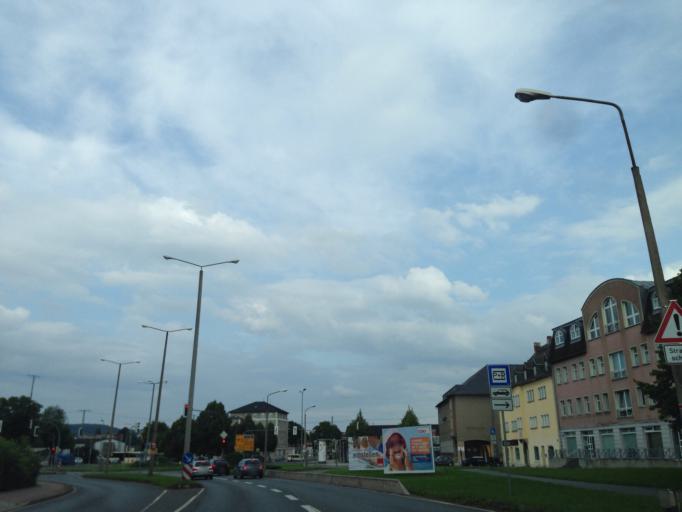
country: DE
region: Thuringia
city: Saalfeld
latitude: 50.6504
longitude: 11.3711
